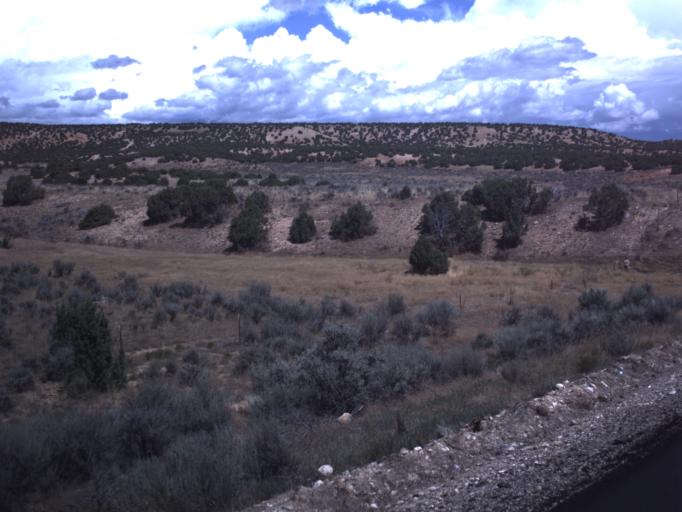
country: US
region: Utah
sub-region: Uintah County
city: Maeser
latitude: 40.4324
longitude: -109.6549
